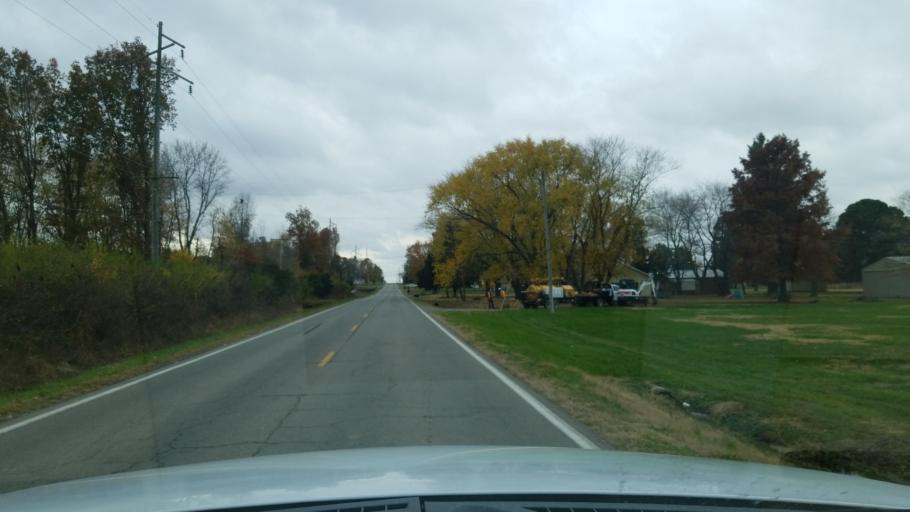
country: US
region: Illinois
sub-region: Saline County
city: Eldorado
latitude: 37.8014
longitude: -88.4383
